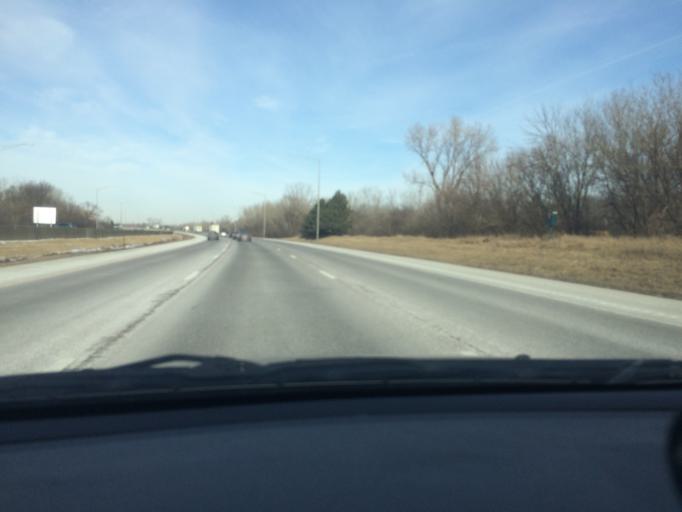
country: US
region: Illinois
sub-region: DuPage County
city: Addison
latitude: 41.9367
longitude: -87.9819
